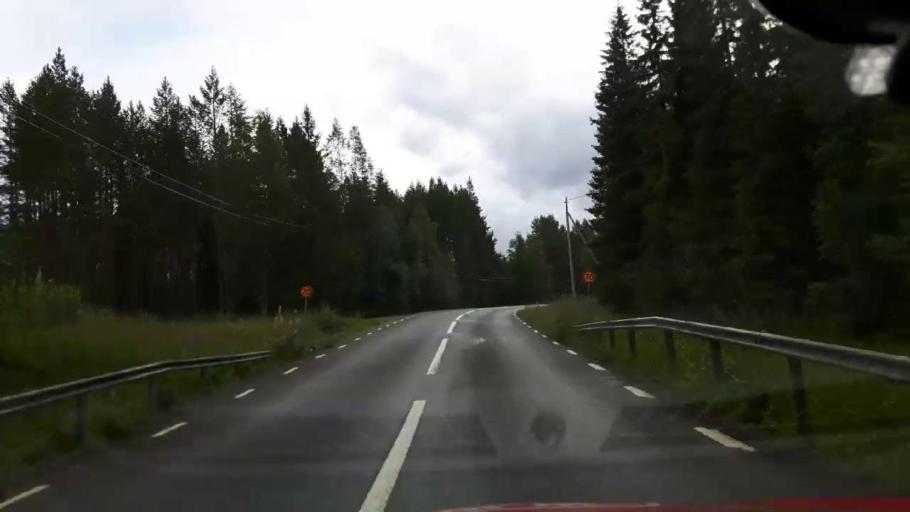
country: NO
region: Nord-Trondelag
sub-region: Lierne
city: Sandvika
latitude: 64.5089
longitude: 14.1575
